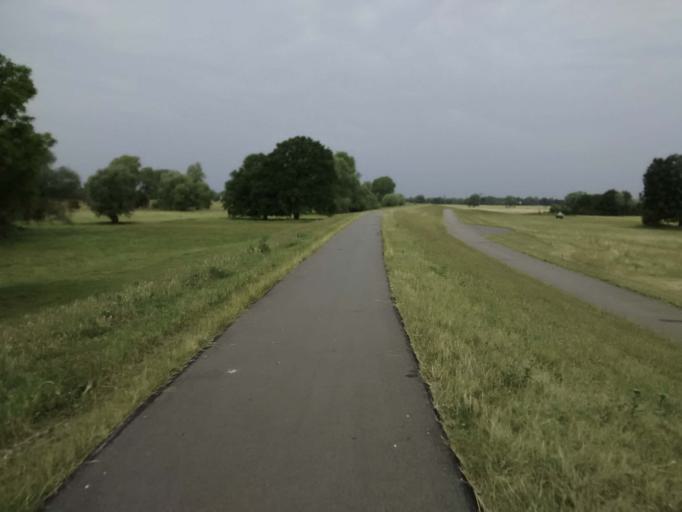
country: DE
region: Brandenburg
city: Breese
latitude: 52.9644
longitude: 11.7913
